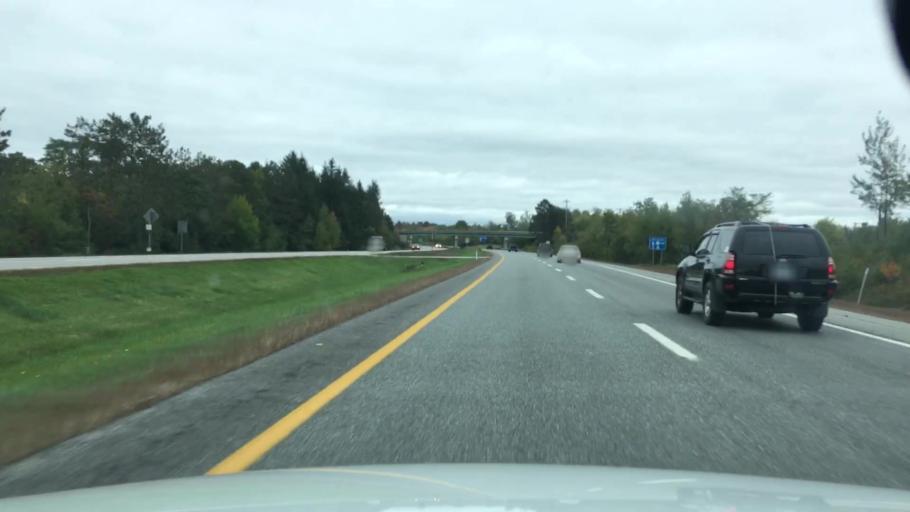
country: US
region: Maine
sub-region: Penobscot County
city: Hampden
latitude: 44.7798
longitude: -68.8220
